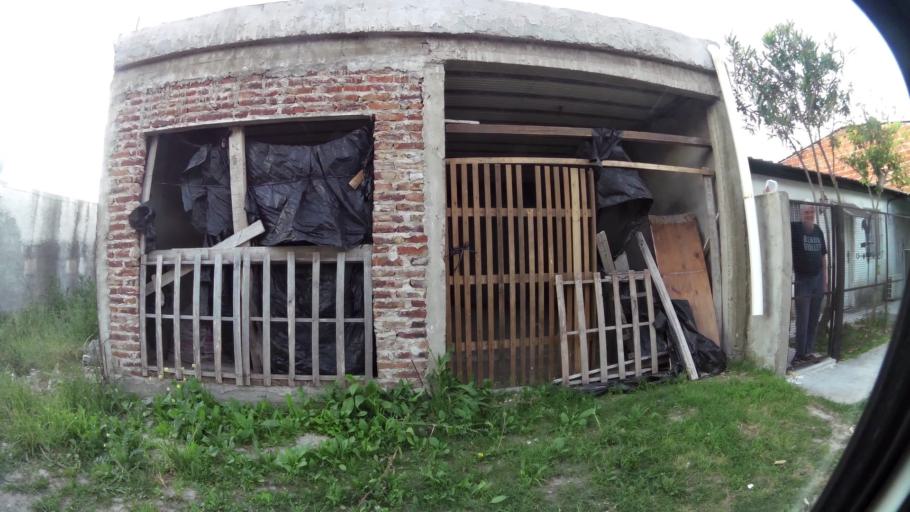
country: AR
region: Buenos Aires
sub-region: Partido de Quilmes
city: Quilmes
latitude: -34.8030
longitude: -58.1813
